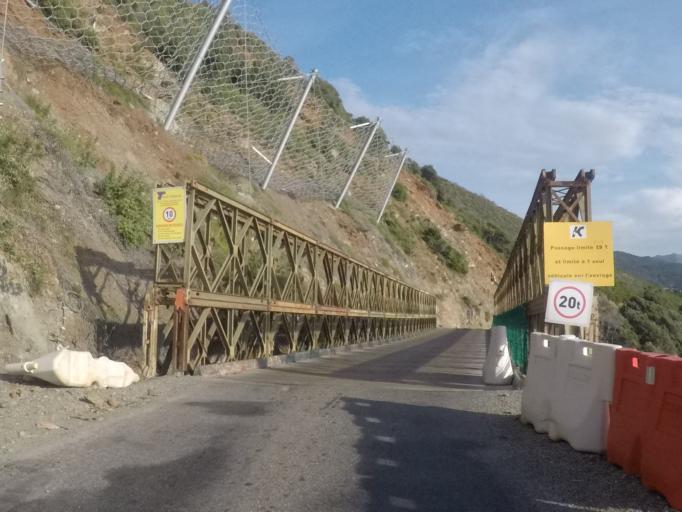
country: FR
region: Corsica
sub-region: Departement de la Haute-Corse
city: Saint-Florent
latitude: 42.7439
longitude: 9.3460
